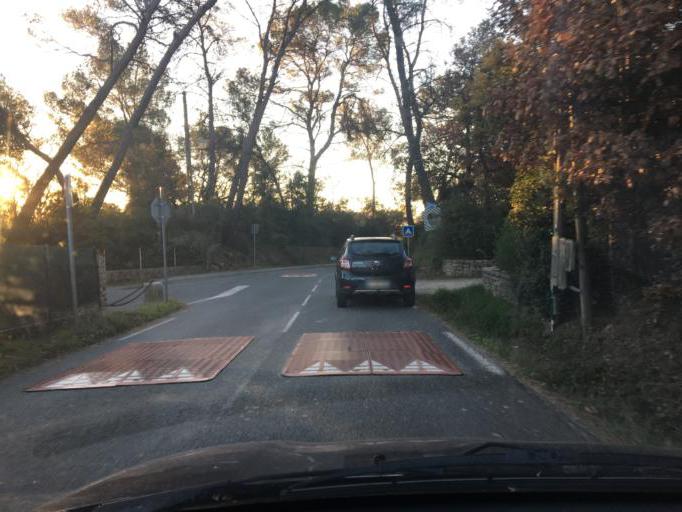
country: FR
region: Provence-Alpes-Cote d'Azur
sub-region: Departement du Var
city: Taradeau
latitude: 43.4546
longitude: 6.4225
